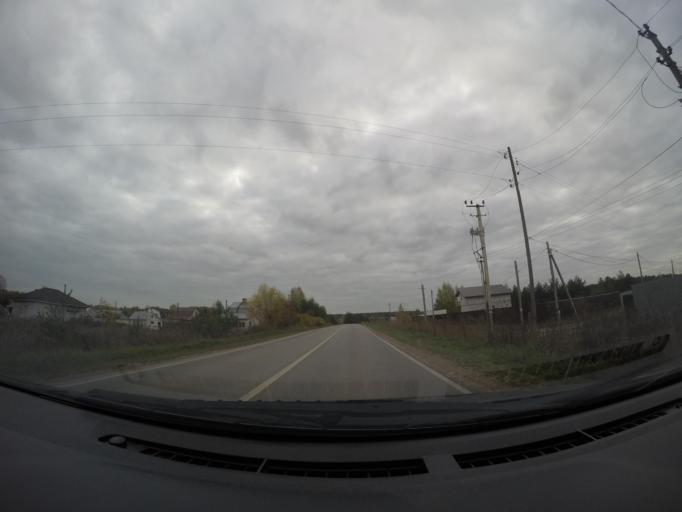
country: RU
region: Moskovskaya
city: Gzhel'
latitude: 55.6435
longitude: 38.4074
